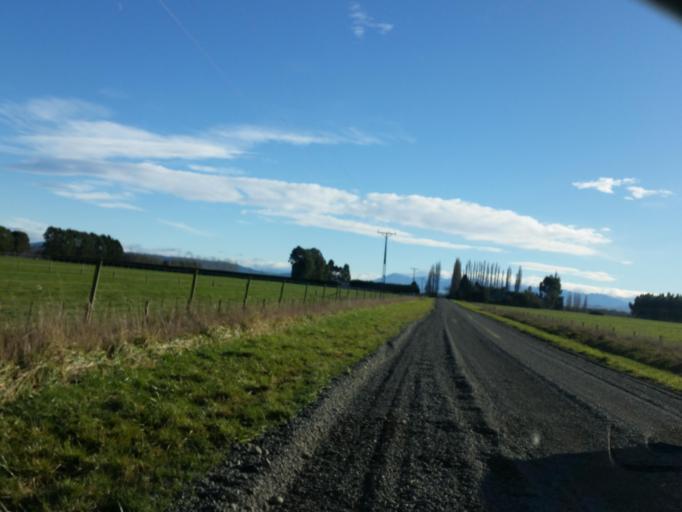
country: NZ
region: Southland
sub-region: Southland District
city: Winton
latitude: -46.0933
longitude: 168.0983
